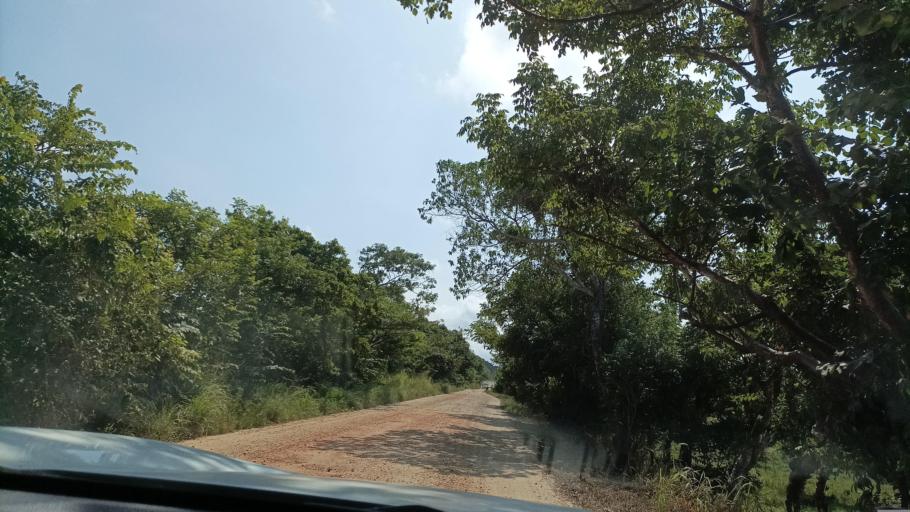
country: MX
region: Veracruz
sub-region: Chinameca
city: Chacalapa
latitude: 18.1265
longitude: -94.6550
